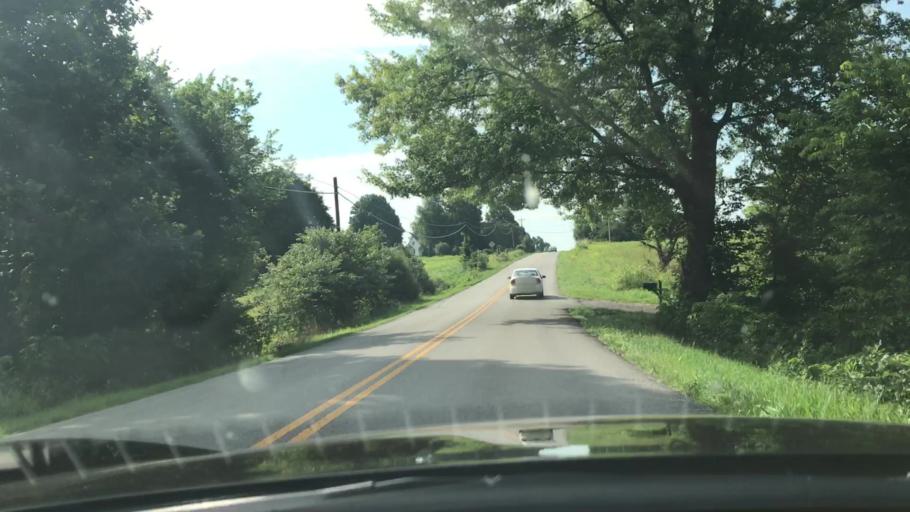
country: US
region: Kentucky
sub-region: Green County
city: Greensburg
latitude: 37.2666
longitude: -85.5630
